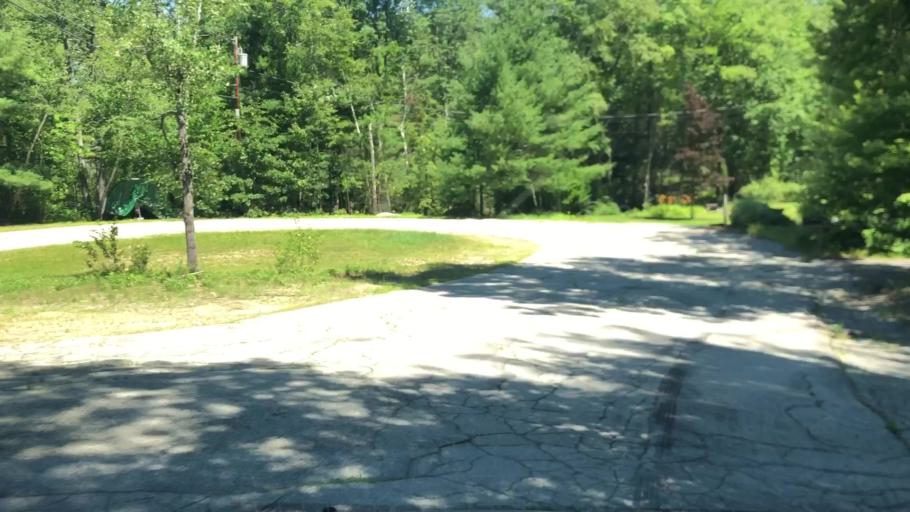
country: US
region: New Hampshire
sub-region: Hillsborough County
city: Milford
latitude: 42.8374
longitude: -71.5862
